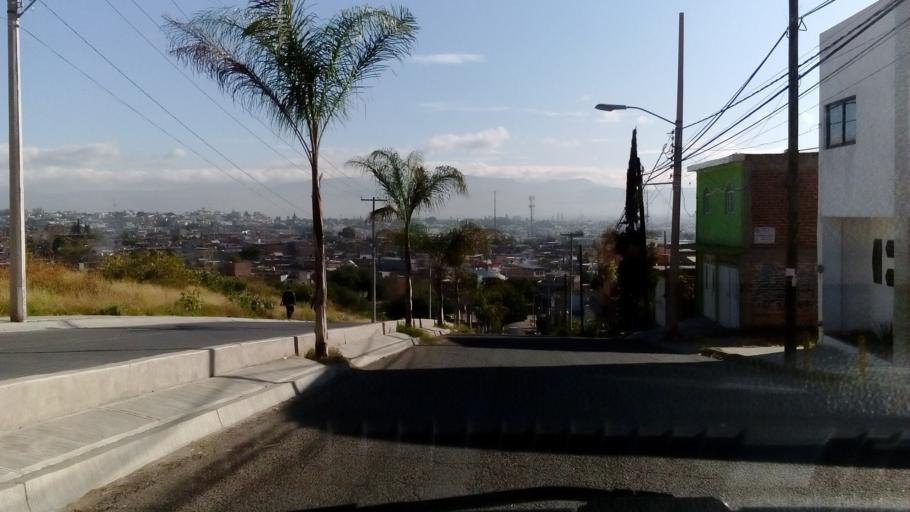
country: MX
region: Guanajuato
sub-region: Leon
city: Ejido la Joya
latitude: 21.1117
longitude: -101.7156
